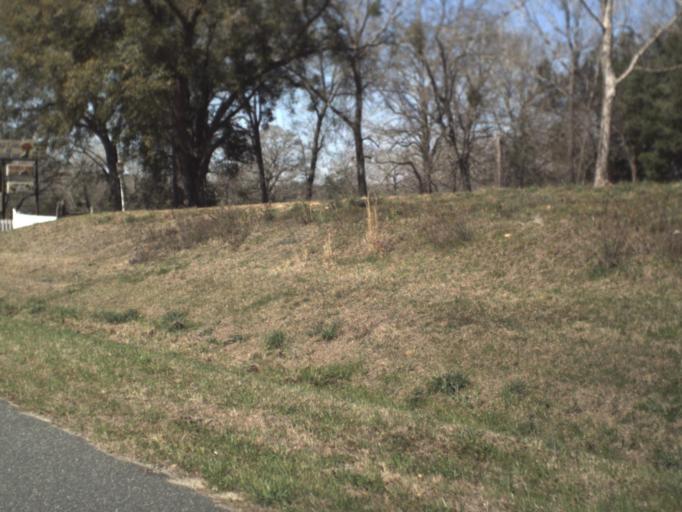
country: US
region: Florida
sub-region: Jackson County
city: Marianna
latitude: 30.7848
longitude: -85.3255
